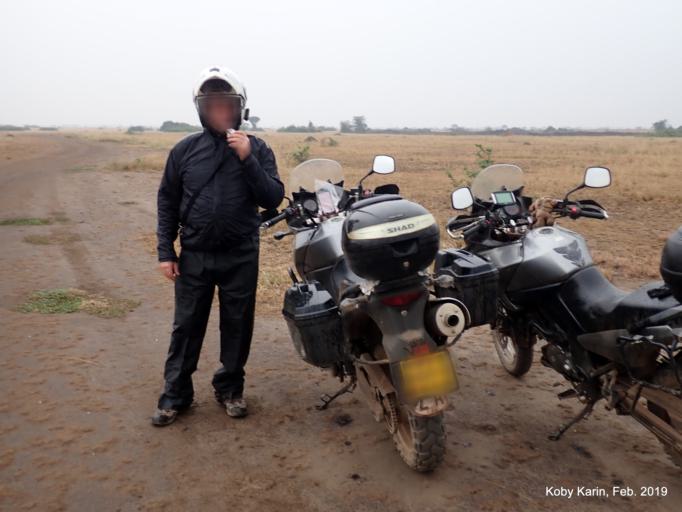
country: UG
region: Western Region
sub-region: Kasese District
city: Kasese
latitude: -0.0331
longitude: 30.0539
